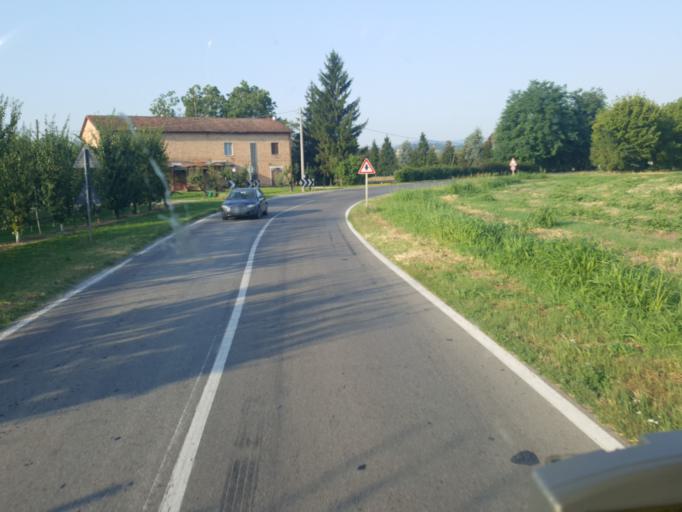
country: IT
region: Emilia-Romagna
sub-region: Provincia di Modena
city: Spilamberto
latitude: 44.5341
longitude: 10.9904
